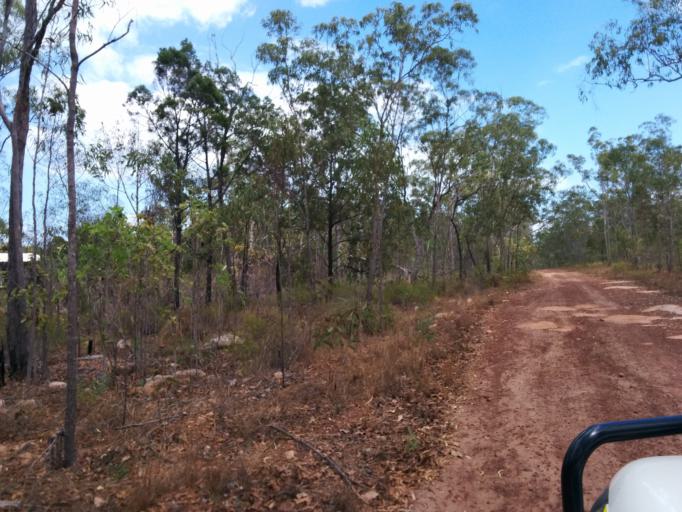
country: AU
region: Northern Territory
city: Alyangula
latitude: -13.8423
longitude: 136.4150
